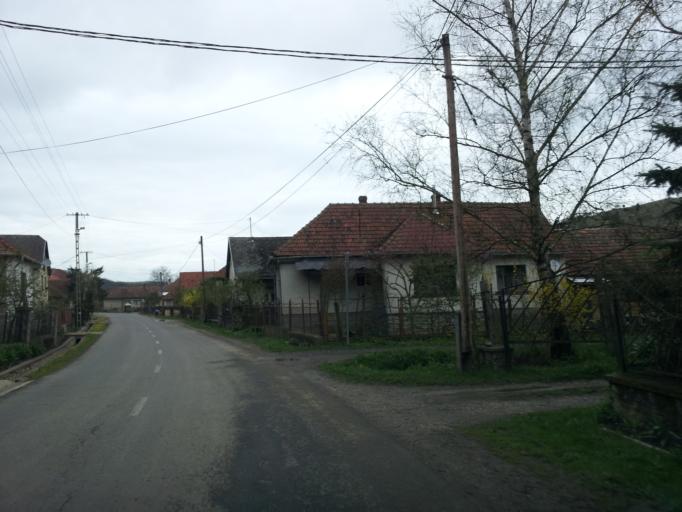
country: HU
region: Borsod-Abauj-Zemplen
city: Rudabanya
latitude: 48.4838
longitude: 20.6239
